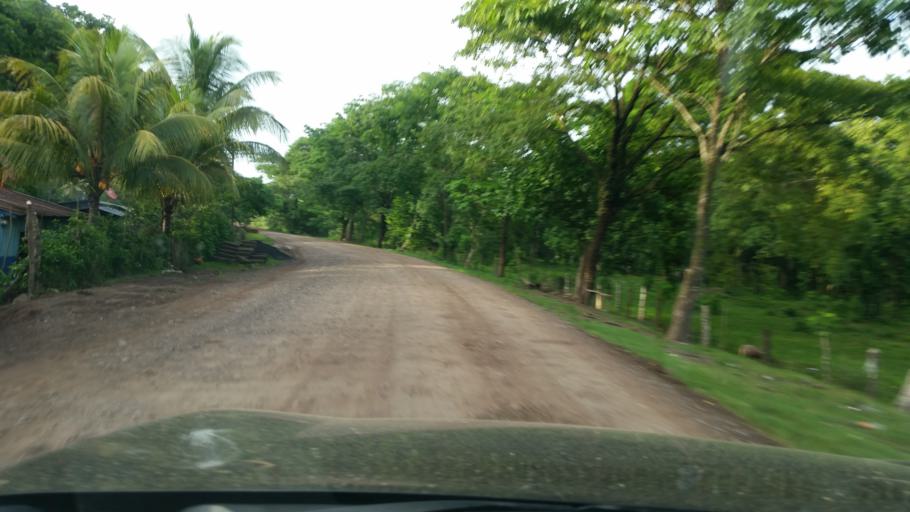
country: NI
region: Atlantico Norte (RAAN)
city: Siuna
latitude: 13.3301
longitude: -84.8909
